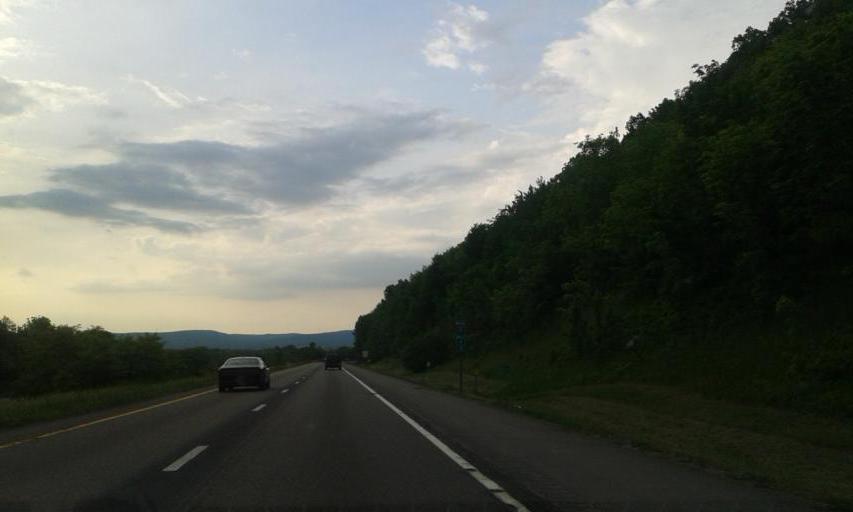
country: US
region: Pennsylvania
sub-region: Susquehanna County
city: Hallstead
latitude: 42.0491
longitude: -75.7961
